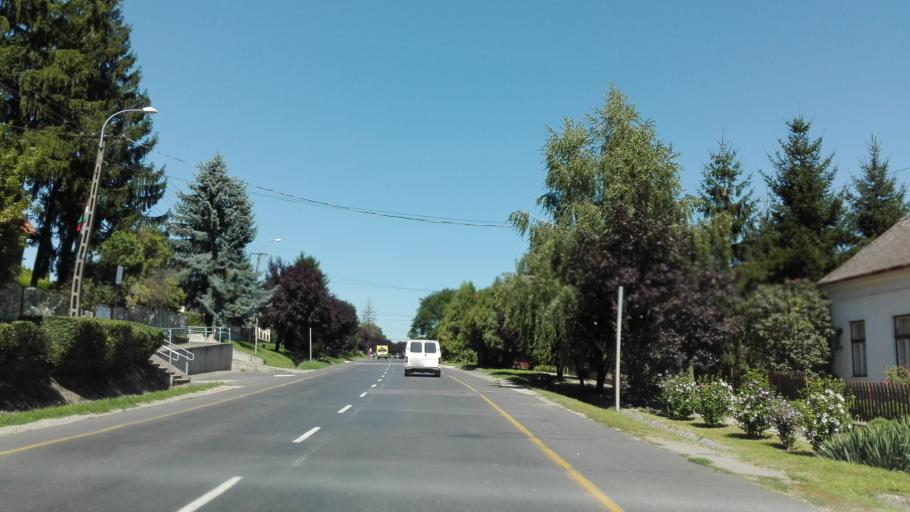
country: HU
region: Fejer
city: Mezoszilas
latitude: 46.8181
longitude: 18.4793
